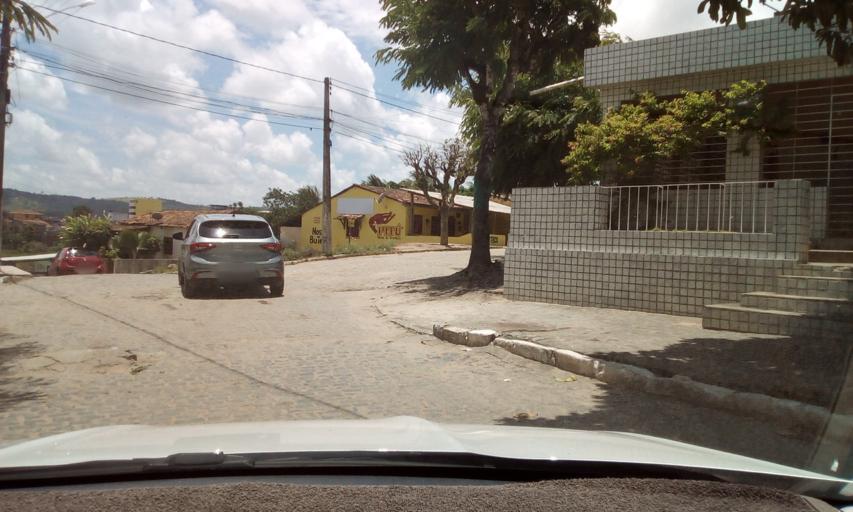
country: BR
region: Pernambuco
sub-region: Bonito
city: Bonito
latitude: -8.4722
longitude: -35.7268
